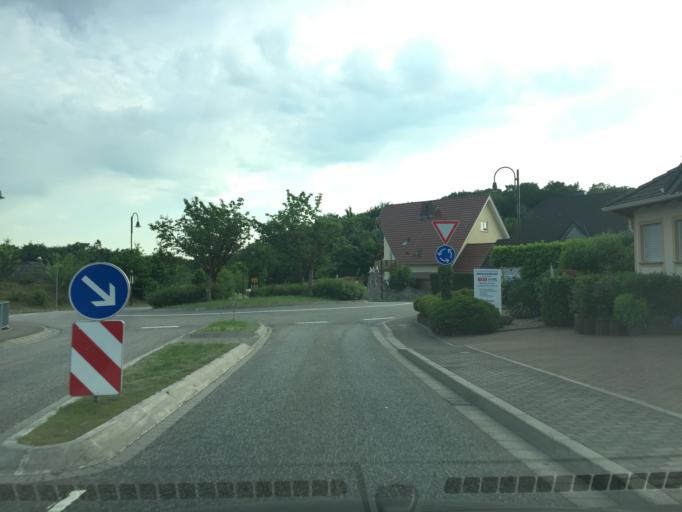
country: DE
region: Rheinland-Pfalz
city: Stromberg
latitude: 50.4523
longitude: 7.5935
